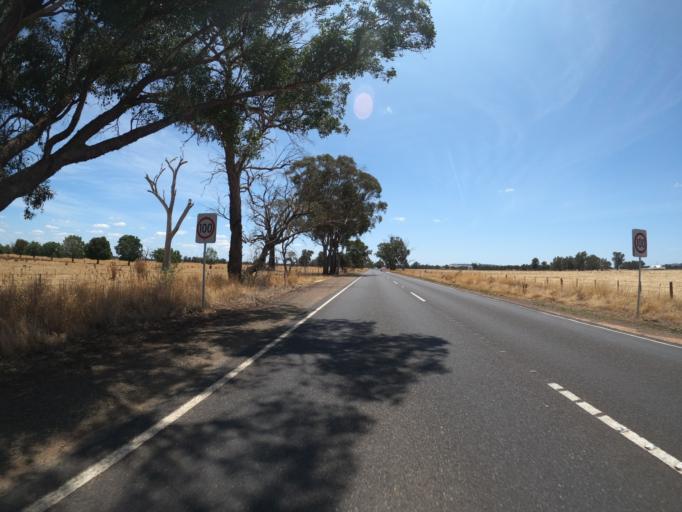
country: AU
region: Victoria
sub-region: Benalla
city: Benalla
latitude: -36.5142
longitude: 146.0308
